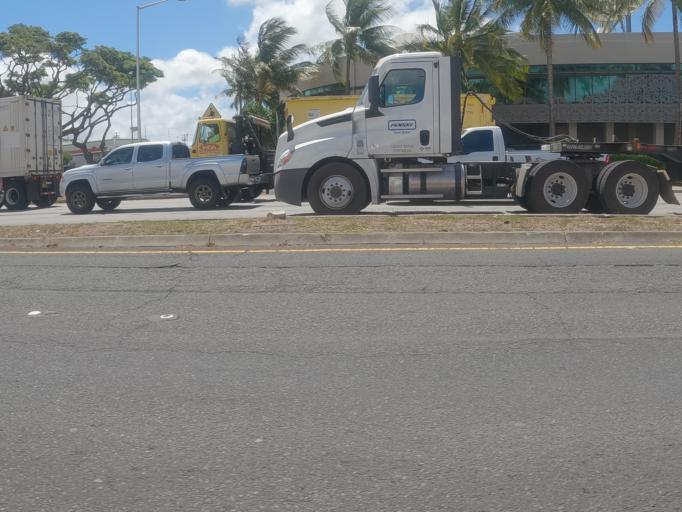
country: US
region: Hawaii
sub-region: Honolulu County
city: Honolulu
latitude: 21.3282
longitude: -157.8873
